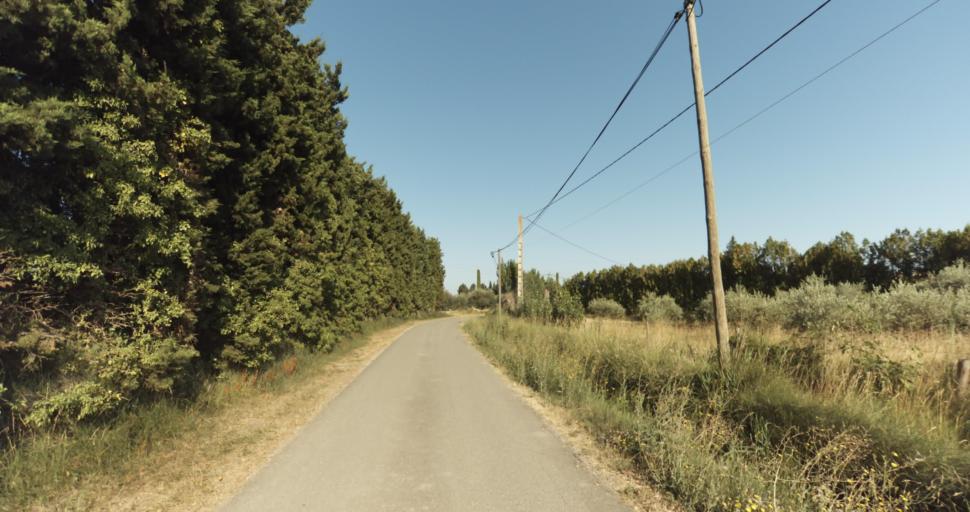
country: FR
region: Provence-Alpes-Cote d'Azur
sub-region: Departement du Vaucluse
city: Monteux
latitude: 44.0487
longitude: 4.9717
